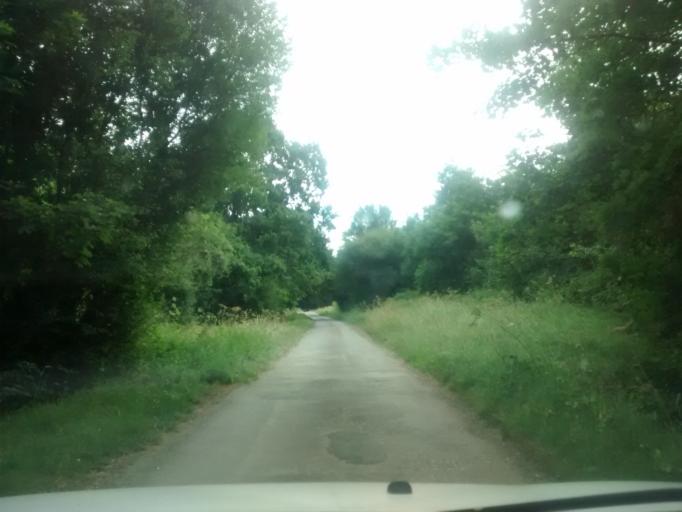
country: FR
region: Brittany
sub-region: Departement d'Ille-et-Vilaine
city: Saint-Jacques-de-la-Lande
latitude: 48.0887
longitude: -1.7235
